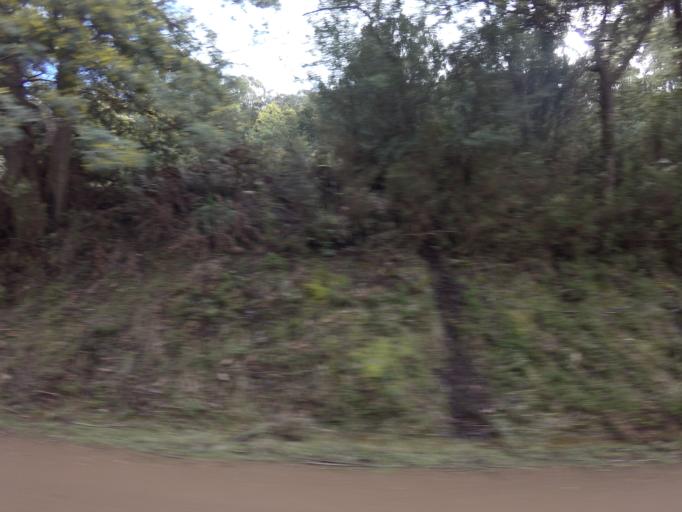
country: AU
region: Tasmania
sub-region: Derwent Valley
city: New Norfolk
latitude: -42.7898
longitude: 146.9322
